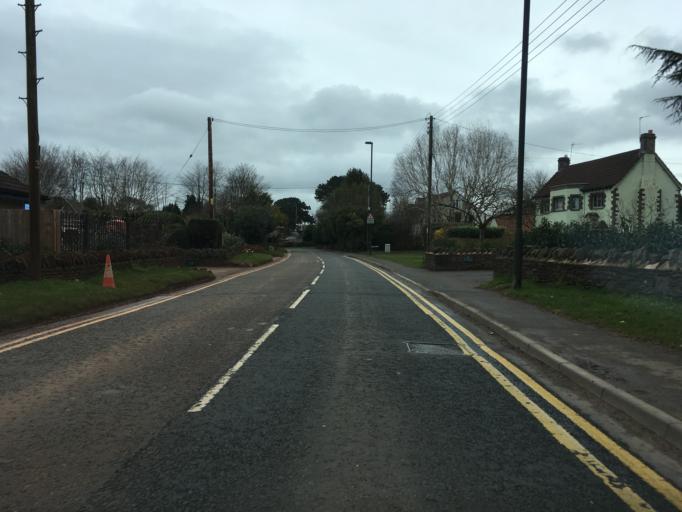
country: GB
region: England
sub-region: South Gloucestershire
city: Stoke Gifford
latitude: 51.5005
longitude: -2.5247
